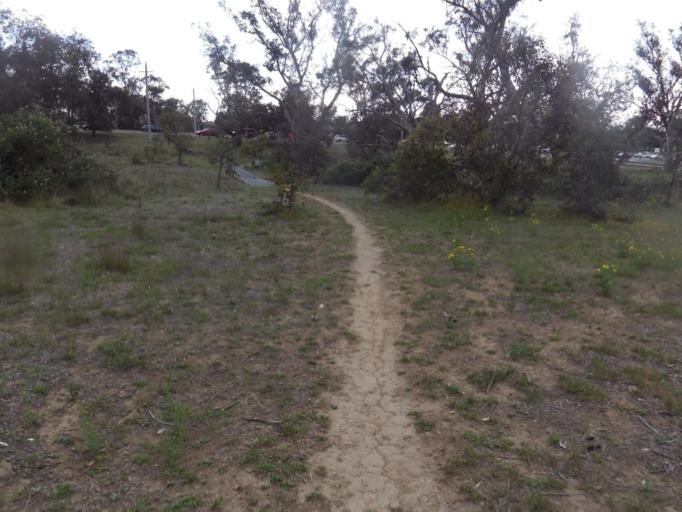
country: AU
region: Australian Capital Territory
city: Forrest
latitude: -35.3452
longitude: 149.1376
